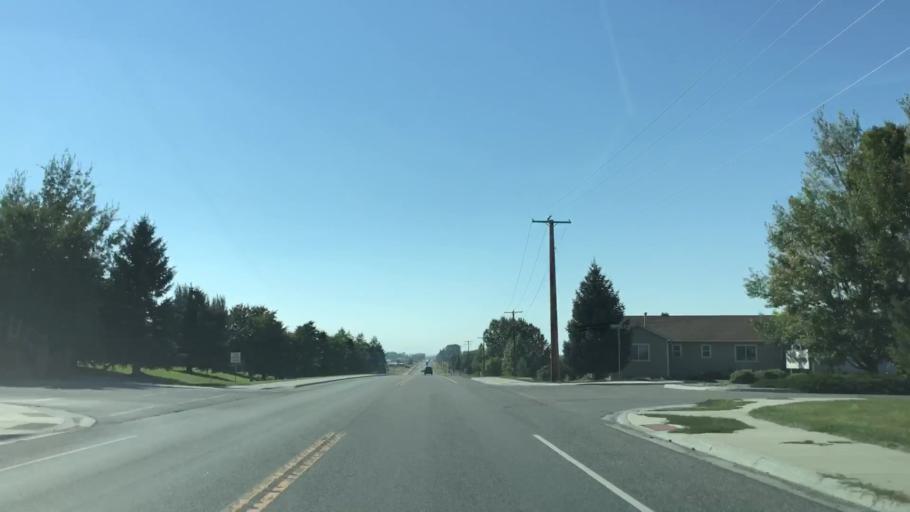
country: US
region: Montana
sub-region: Gallatin County
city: Belgrade
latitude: 45.7293
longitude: -111.1363
